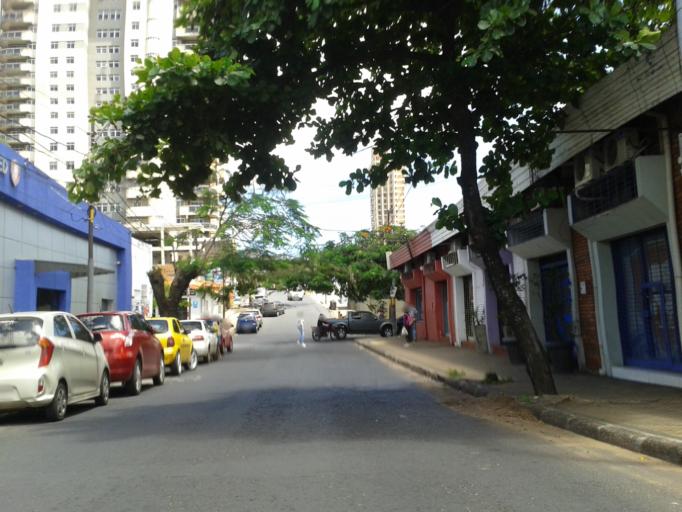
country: PY
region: Asuncion
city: Asuncion
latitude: -25.2901
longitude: -57.6207
